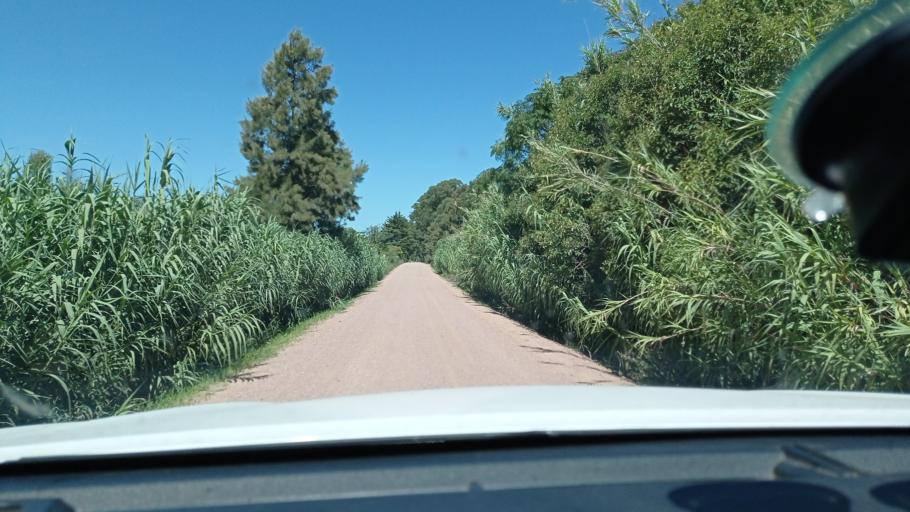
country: UY
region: Canelones
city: La Paz
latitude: -34.7569
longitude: -56.1848
